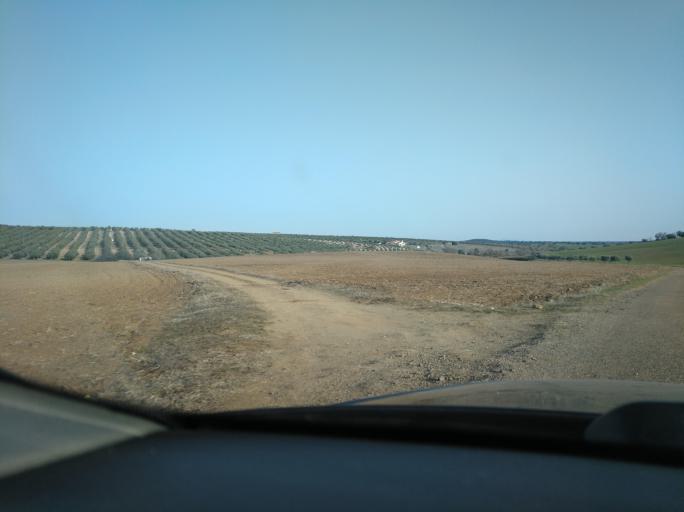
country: PT
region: Portalegre
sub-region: Campo Maior
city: Campo Maior
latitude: 39.0069
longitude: -7.0216
